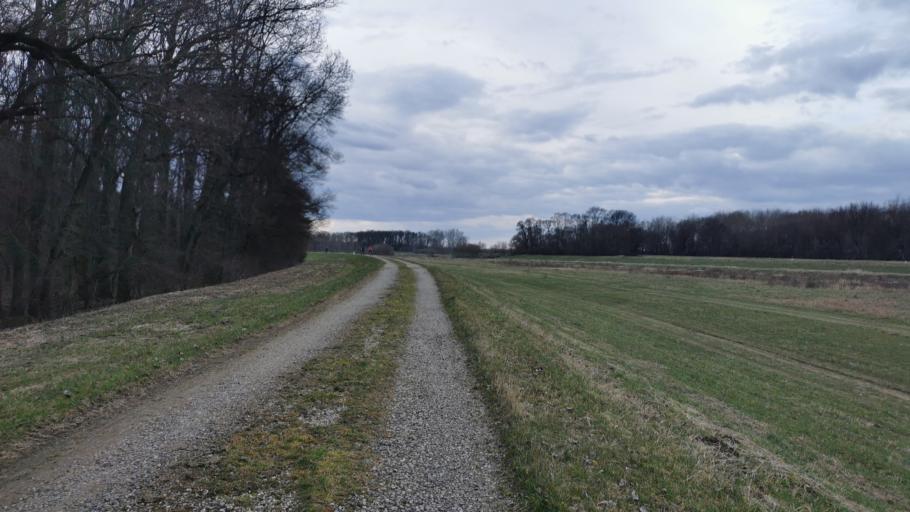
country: CZ
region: South Moravian
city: Hodonin
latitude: 48.8317
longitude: 17.1136
